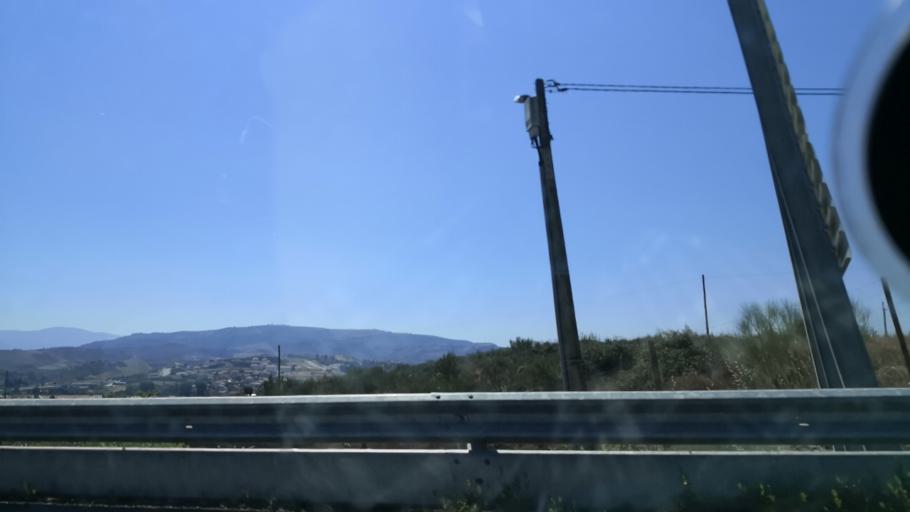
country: PT
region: Braganca
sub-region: Mirandela
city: Mirandela
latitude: 41.4990
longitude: -7.1862
